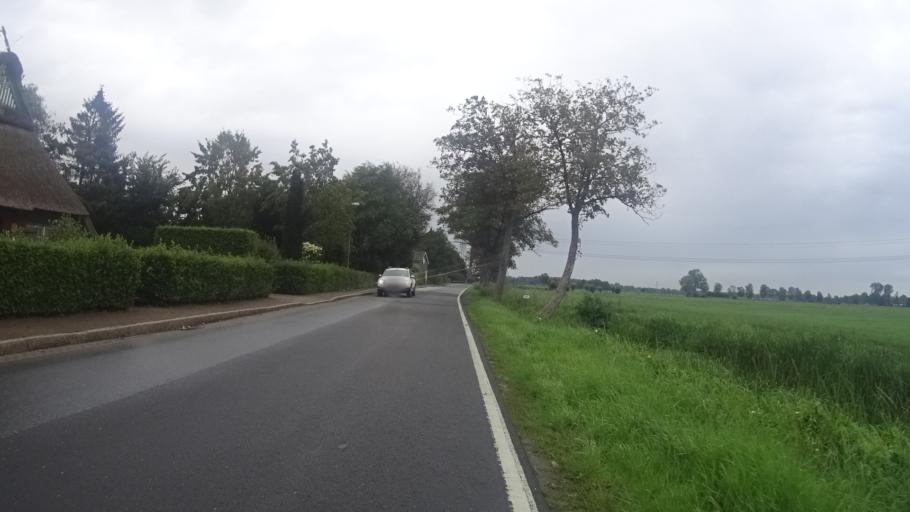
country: DE
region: Schleswig-Holstein
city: Altenmoor
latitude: 53.7909
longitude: 9.5816
